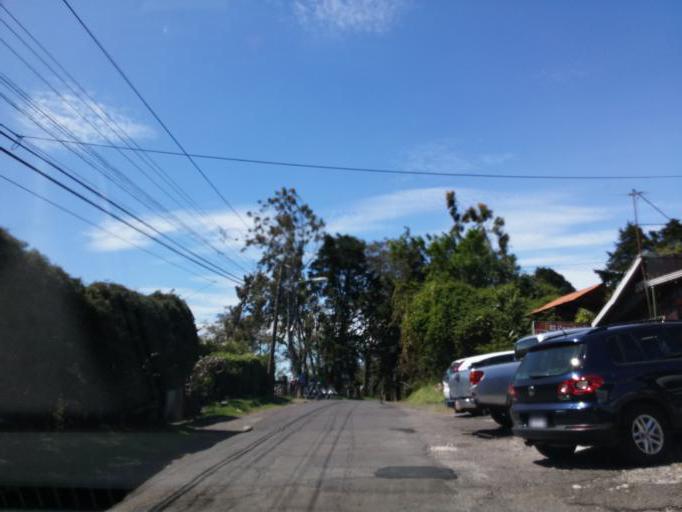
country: CR
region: Heredia
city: Santo Domingo
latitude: 10.0924
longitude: -84.1095
